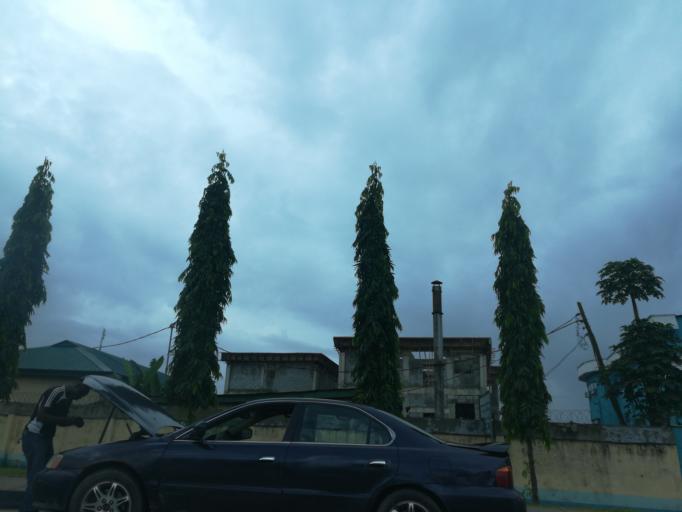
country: NG
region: Lagos
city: Ikeja
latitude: 6.5866
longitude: 3.3337
